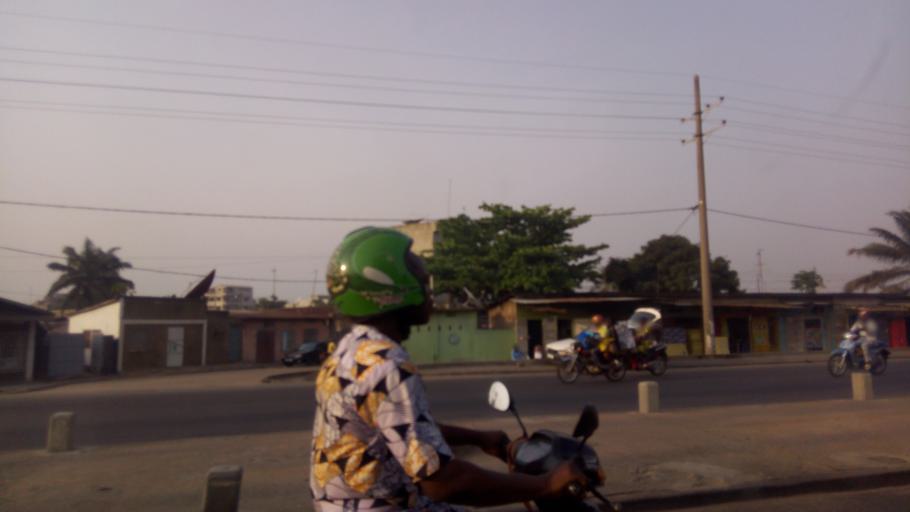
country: BJ
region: Littoral
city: Cotonou
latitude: 6.3766
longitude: 2.3990
